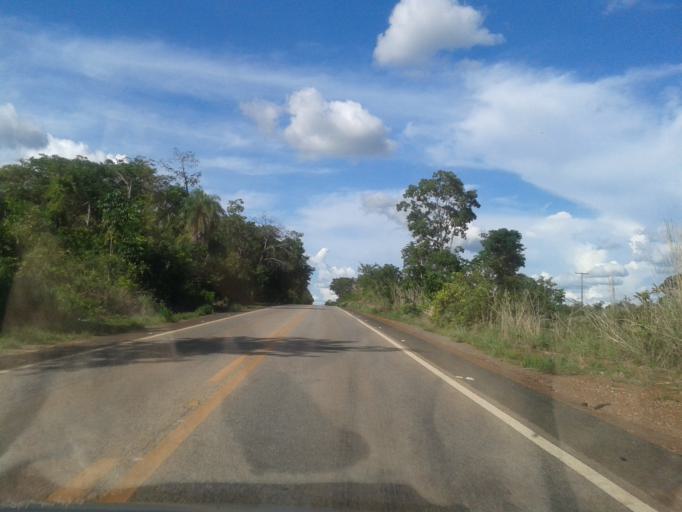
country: BR
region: Goias
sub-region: Mozarlandia
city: Mozarlandia
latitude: -14.6836
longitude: -50.5398
